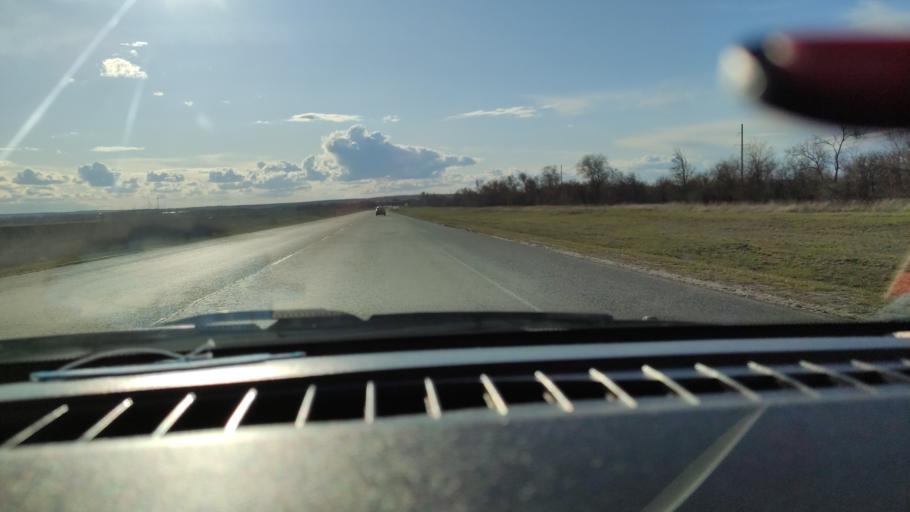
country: RU
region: Saratov
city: Yelshanka
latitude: 51.8299
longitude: 46.2439
